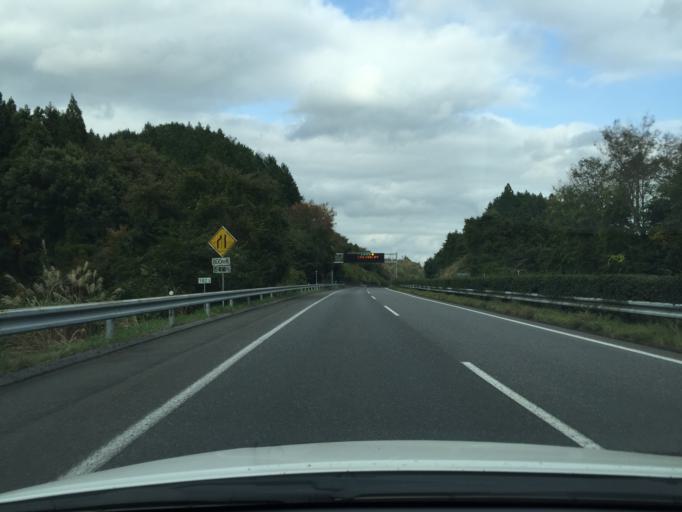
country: JP
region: Fukushima
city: Iwaki
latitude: 36.9640
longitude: 140.7839
